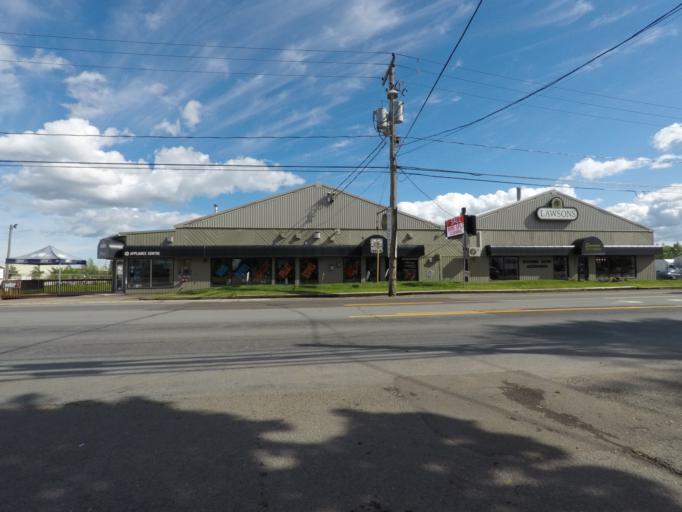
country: CA
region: New Brunswick
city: Moncton
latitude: 46.0969
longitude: -64.8207
